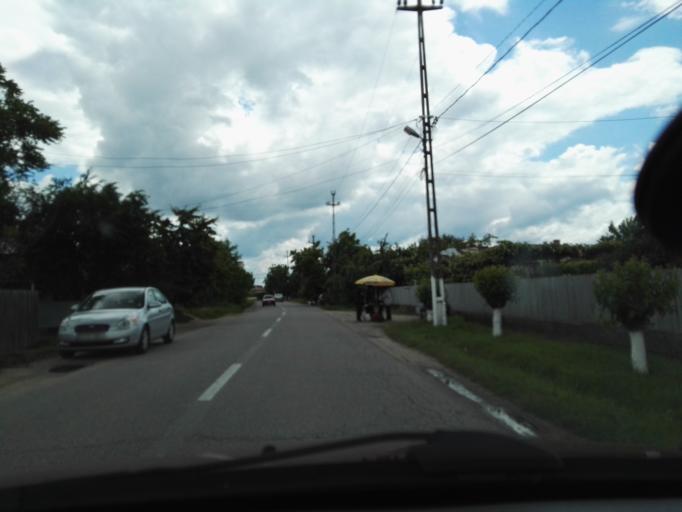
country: RO
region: Ilfov
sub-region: Comuna Copaceni
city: Copaceni
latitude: 44.2382
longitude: 26.1101
